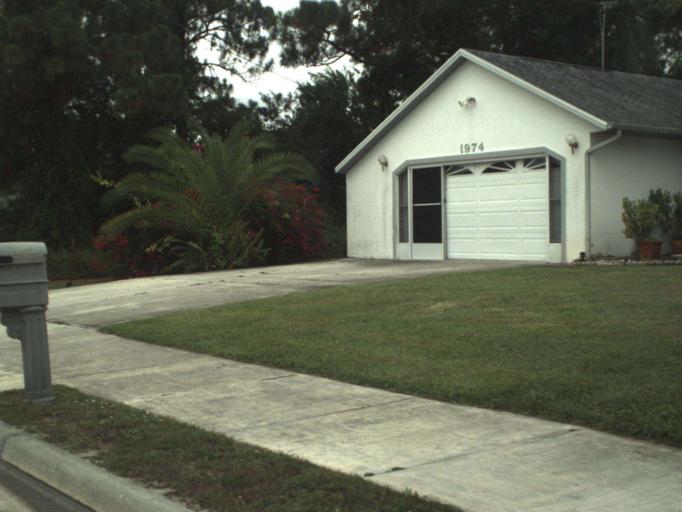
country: US
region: Florida
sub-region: Saint Lucie County
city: Port Saint Lucie
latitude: 27.2826
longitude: -80.3435
